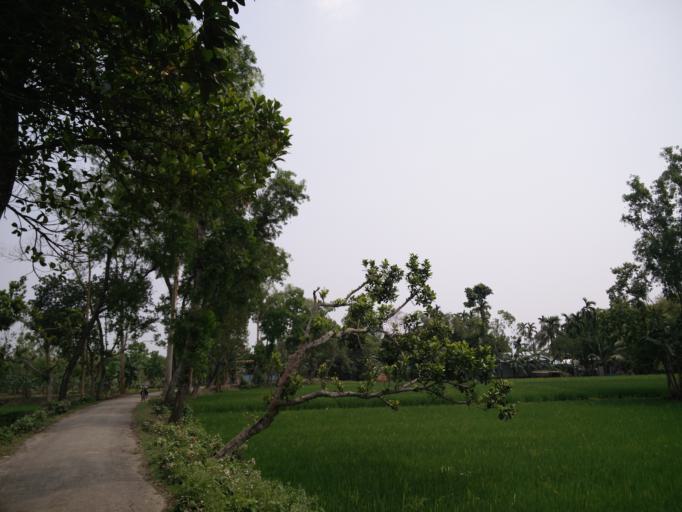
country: BD
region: Dhaka
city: Sherpur
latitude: 24.9339
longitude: 90.1633
